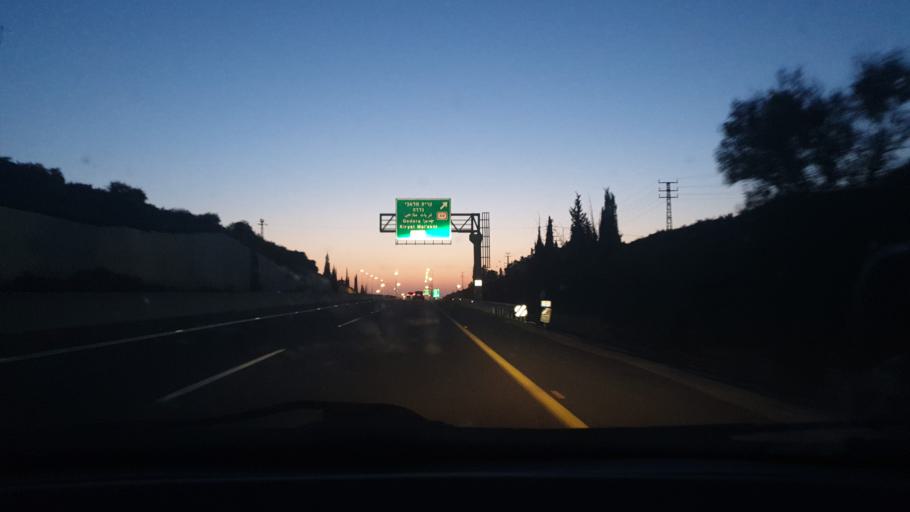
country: IL
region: Central District
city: Gedera
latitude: 31.7999
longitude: 34.7773
